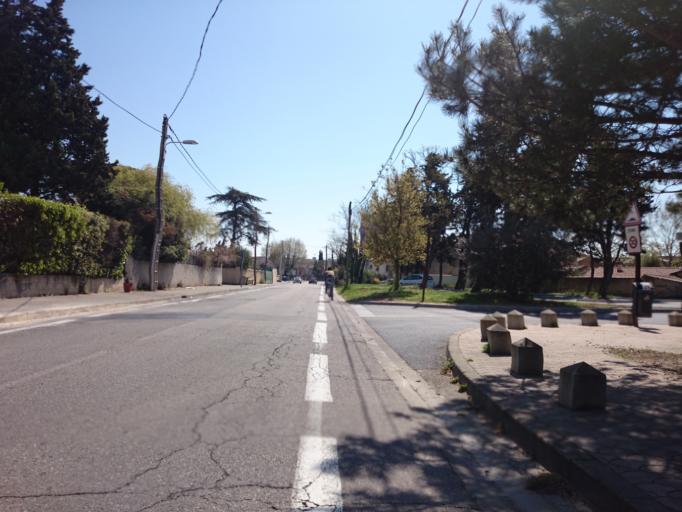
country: FR
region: Provence-Alpes-Cote d'Azur
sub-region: Departement du Vaucluse
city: Avignon
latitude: 43.9305
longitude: 4.7976
